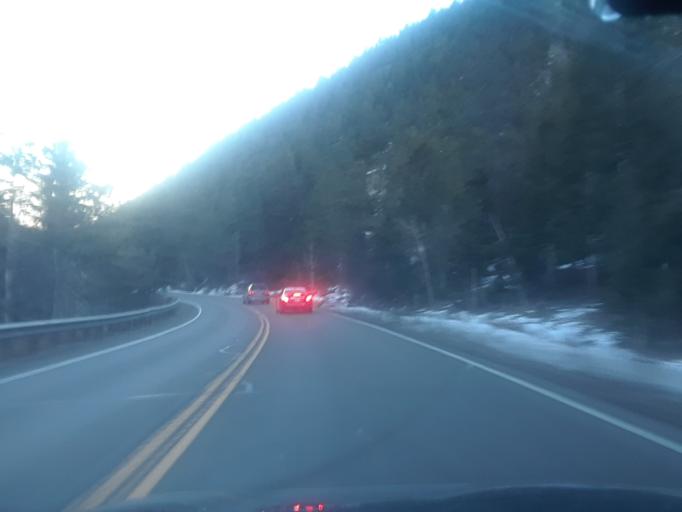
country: US
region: Colorado
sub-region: Clear Creek County
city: Georgetown
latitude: 39.4473
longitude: -105.6195
